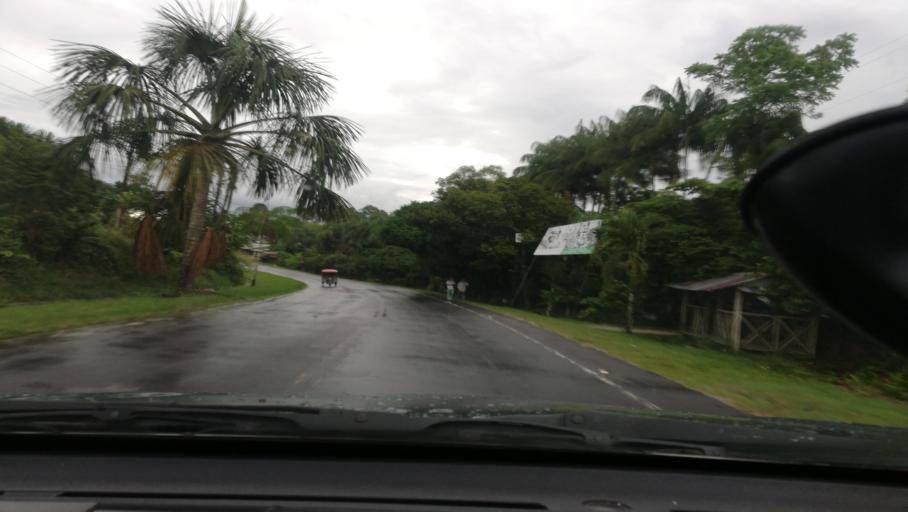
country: PE
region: Loreto
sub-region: Provincia de Maynas
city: Iquitos
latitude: -3.8837
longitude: -73.3510
